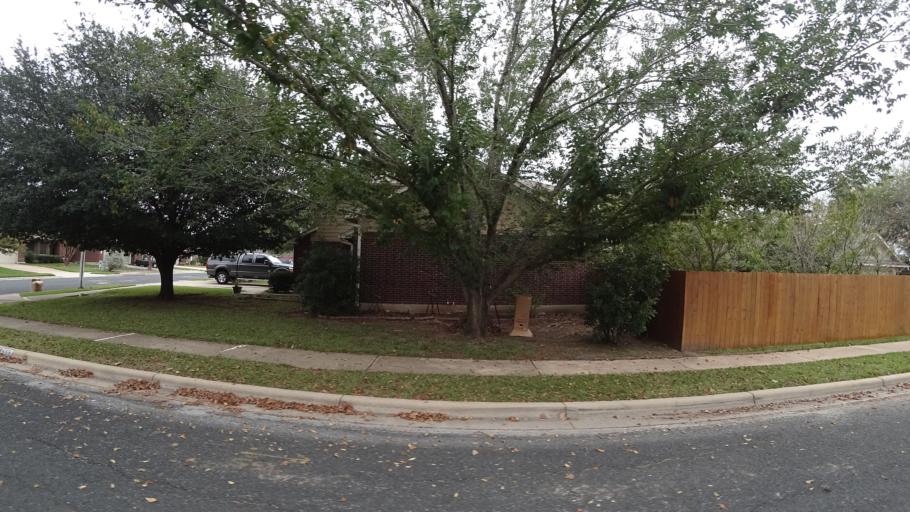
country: US
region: Texas
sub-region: Travis County
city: Shady Hollow
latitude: 30.1515
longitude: -97.8518
